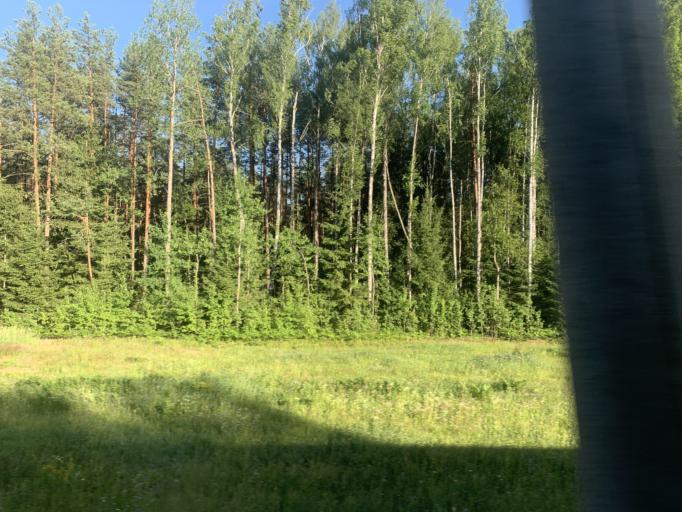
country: BY
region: Minsk
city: Enyerhyetykaw
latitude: 53.5340
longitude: 26.9431
